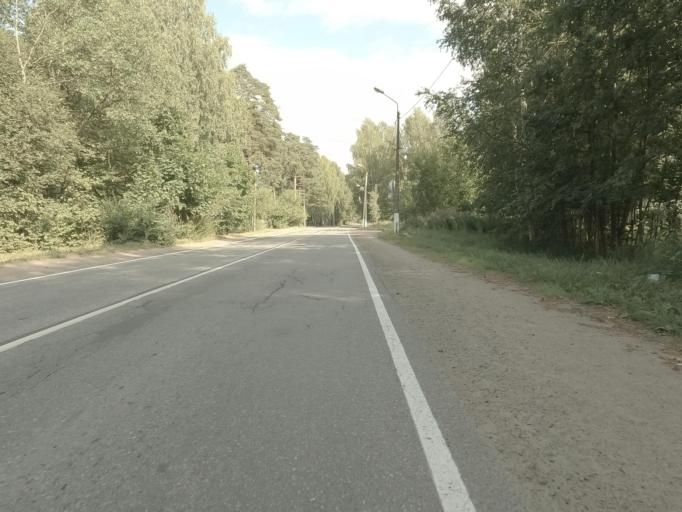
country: RU
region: Leningrad
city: Kamennogorsk
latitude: 60.9470
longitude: 29.1366
